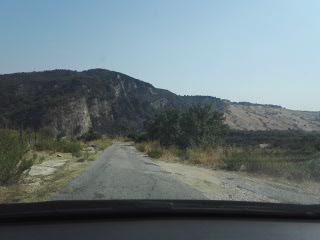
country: IT
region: Calabria
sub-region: Provincia di Reggio Calabria
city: Camini
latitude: 38.4449
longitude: 16.4710
